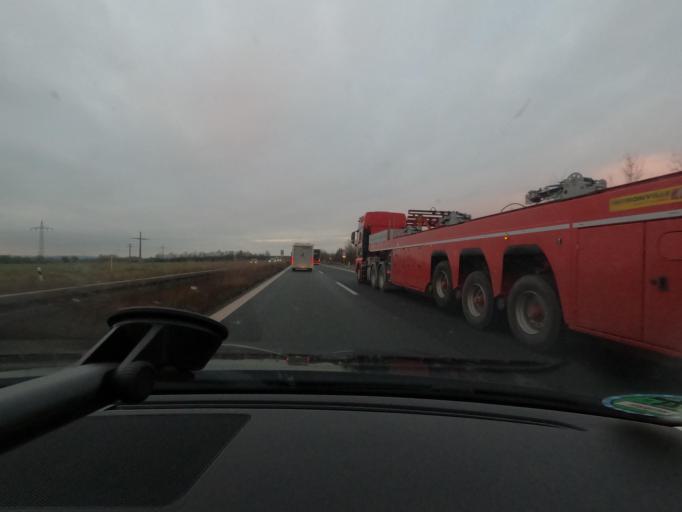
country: DE
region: Bavaria
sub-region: Upper Franconia
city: Eggolsheim
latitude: 49.7811
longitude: 11.0405
